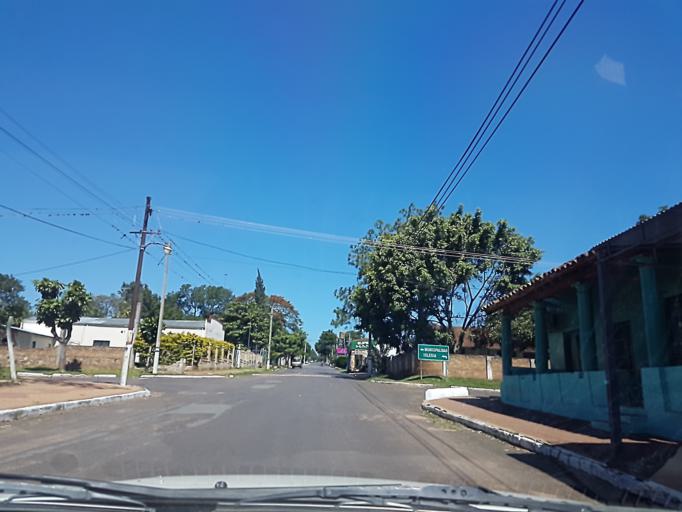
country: PY
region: Cordillera
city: Atyra
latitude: -25.2792
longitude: -57.1731
